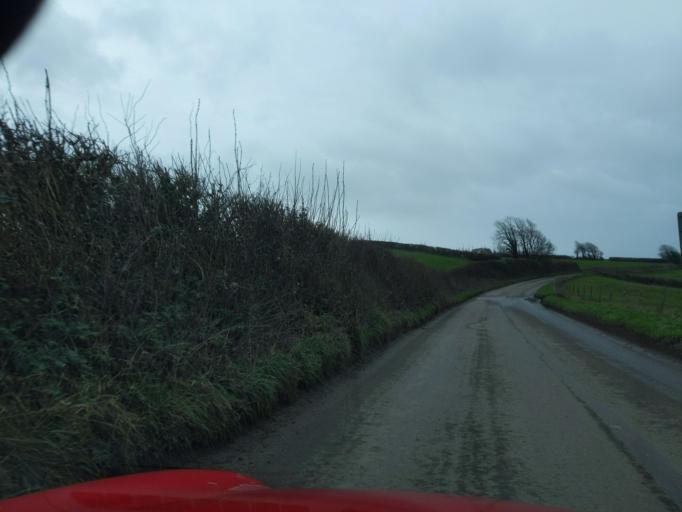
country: GB
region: England
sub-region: Devon
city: Modbury
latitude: 50.3349
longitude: -3.8689
